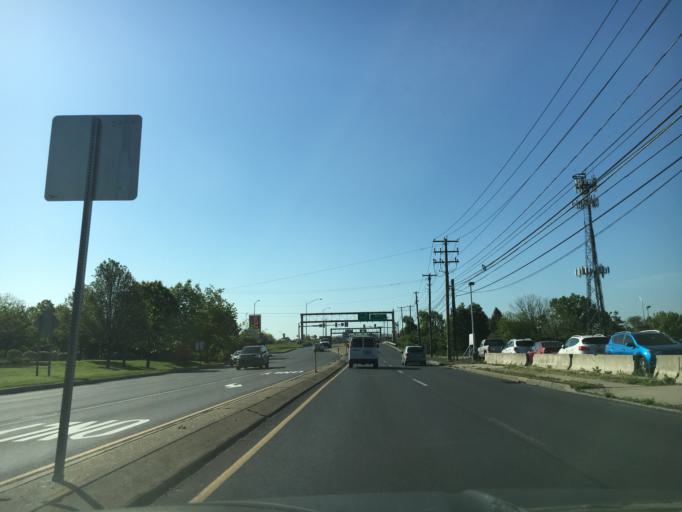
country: US
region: Pennsylvania
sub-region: Northampton County
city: Bethlehem
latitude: 40.6519
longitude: -75.4129
